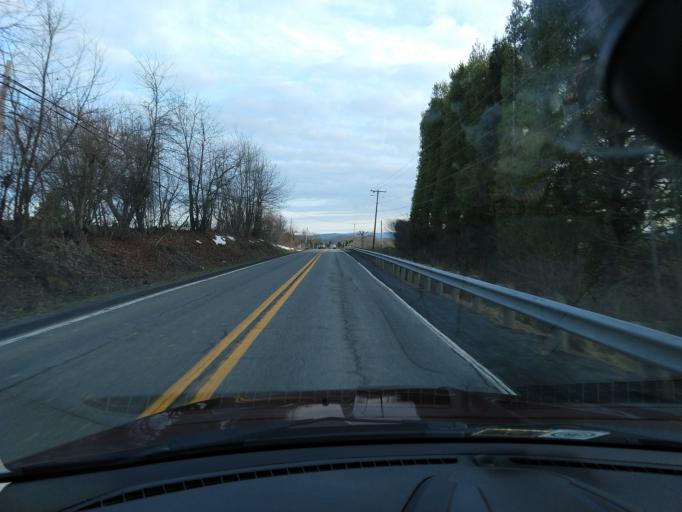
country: US
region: West Virginia
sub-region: Greenbrier County
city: Lewisburg
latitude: 37.9118
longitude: -80.3842
